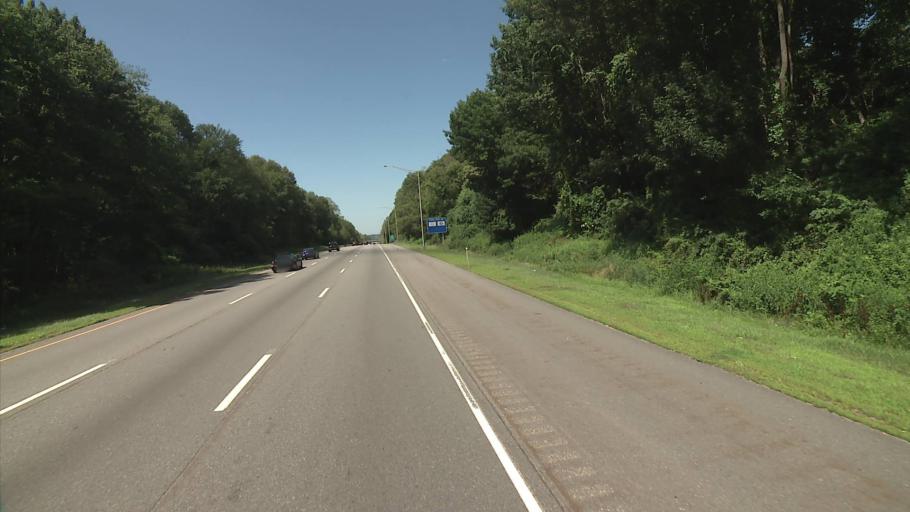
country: US
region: Connecticut
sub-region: New London County
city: Poquonock Bridge
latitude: 41.3706
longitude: -72.0004
